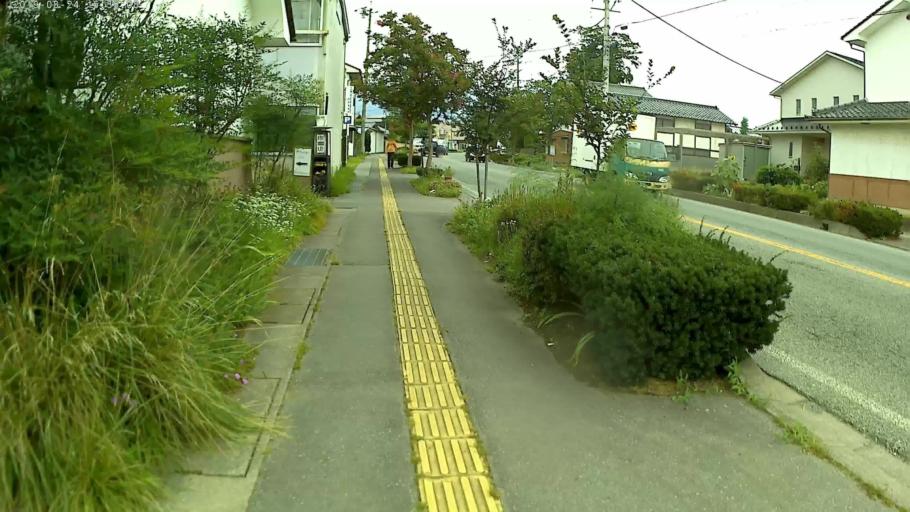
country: JP
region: Nagano
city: Komoro
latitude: 36.2780
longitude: 138.4783
